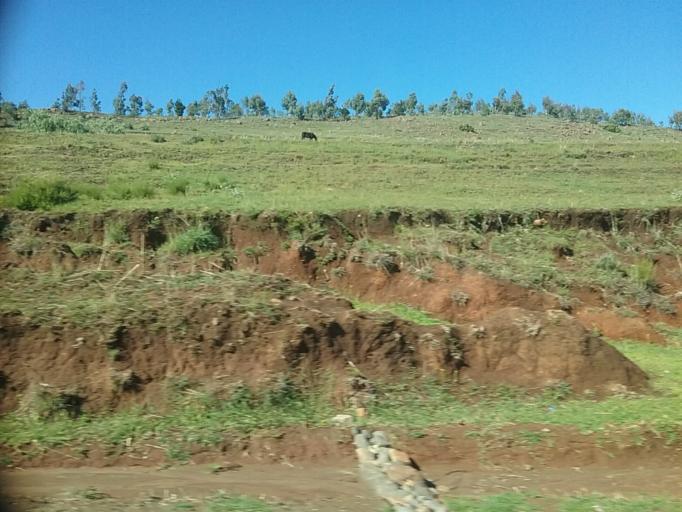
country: LS
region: Berea
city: Teyateyaneng
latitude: -29.2317
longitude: 27.8902
